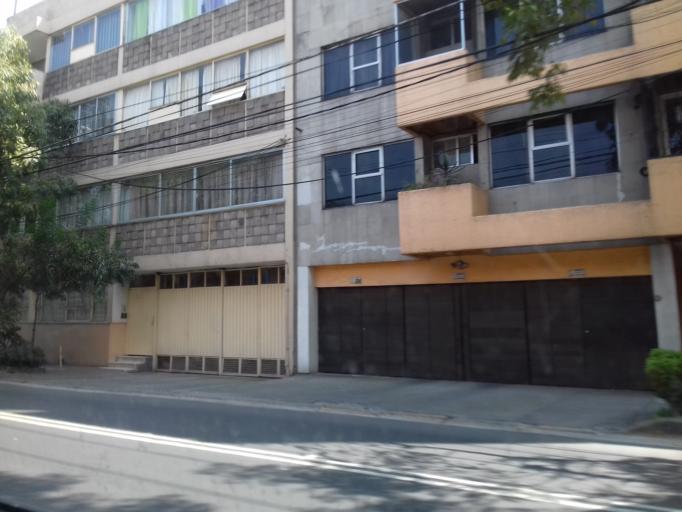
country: MX
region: Mexico City
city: Colonia del Valle
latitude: 19.3744
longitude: -99.1672
